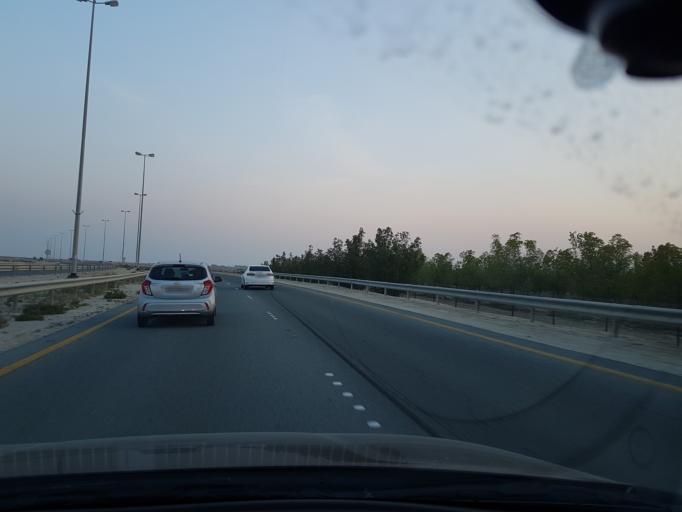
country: BH
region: Central Governorate
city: Dar Kulayb
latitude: 26.0124
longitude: 50.4836
